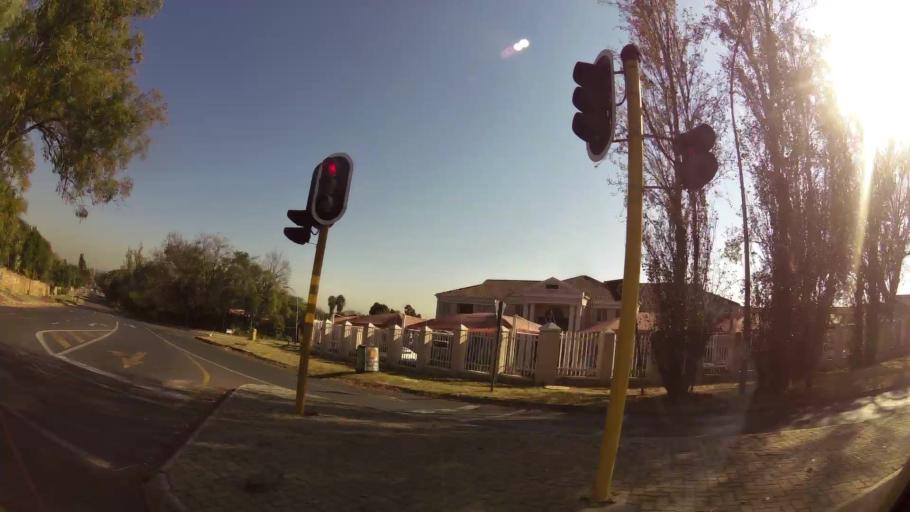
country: ZA
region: Gauteng
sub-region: Ekurhuleni Metropolitan Municipality
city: Germiston
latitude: -26.1687
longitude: 28.1573
